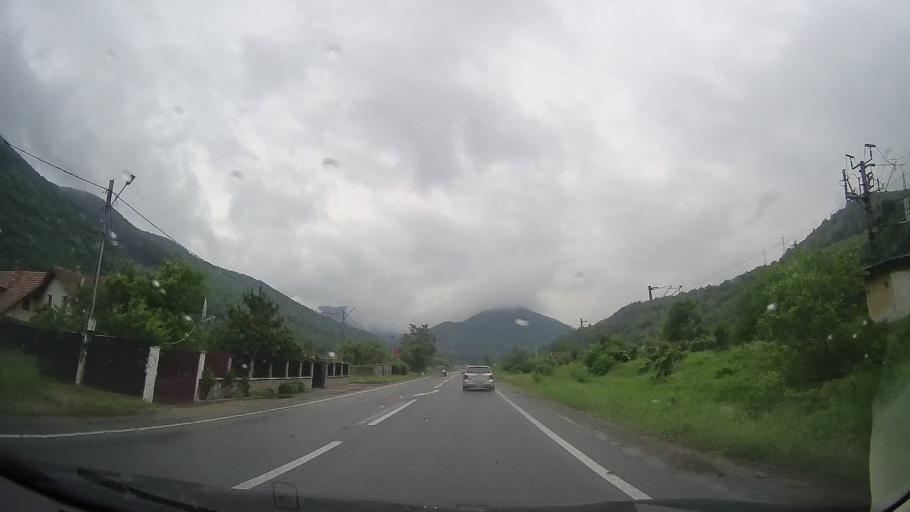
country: RO
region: Caras-Severin
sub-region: Oras Baile Herculane
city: Baile Herculane
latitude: 44.8740
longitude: 22.3854
